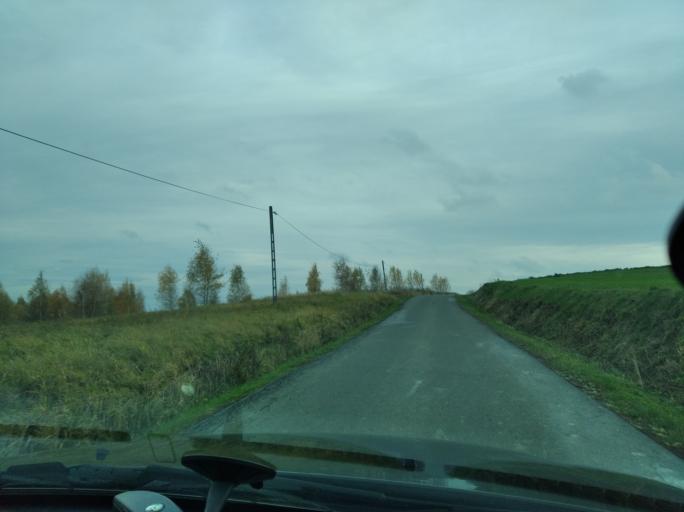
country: PL
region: Subcarpathian Voivodeship
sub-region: Powiat strzyzowski
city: Strzyzow
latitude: 49.9142
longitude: 21.7692
